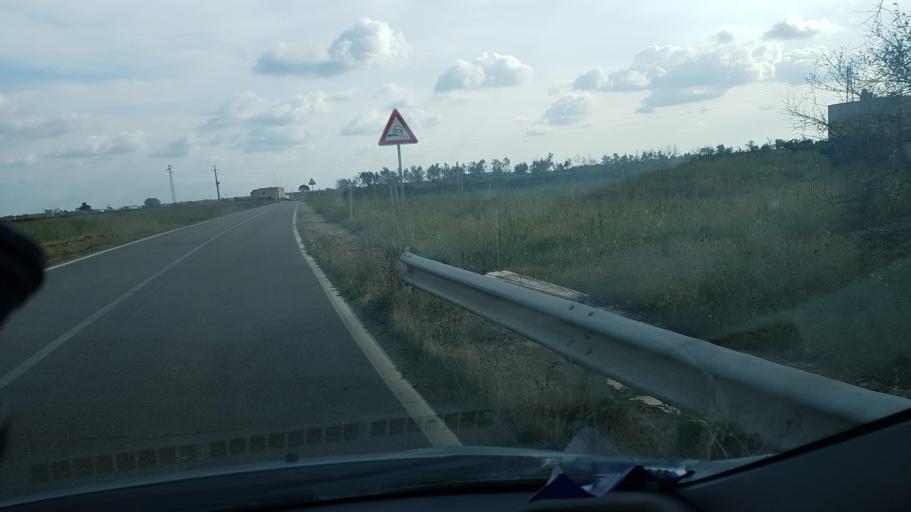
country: IT
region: Apulia
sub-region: Provincia di Brindisi
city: Cellino San Marco
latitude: 40.4430
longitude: 17.9549
